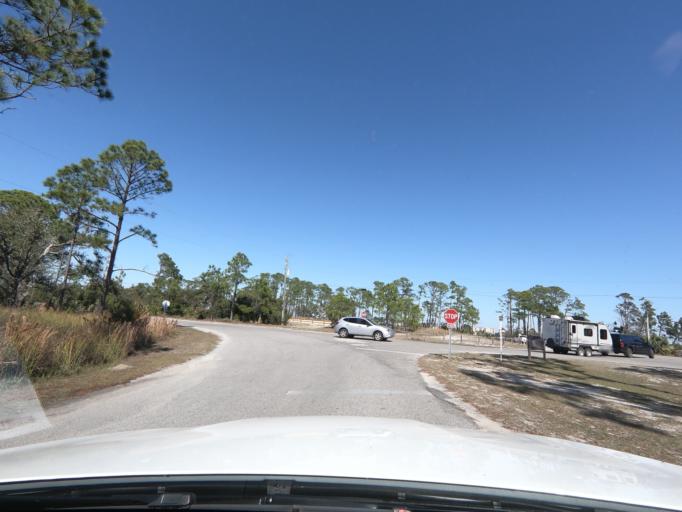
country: US
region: Florida
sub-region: Bay County
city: Lower Grand Lagoon
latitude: 30.1309
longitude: -85.7327
